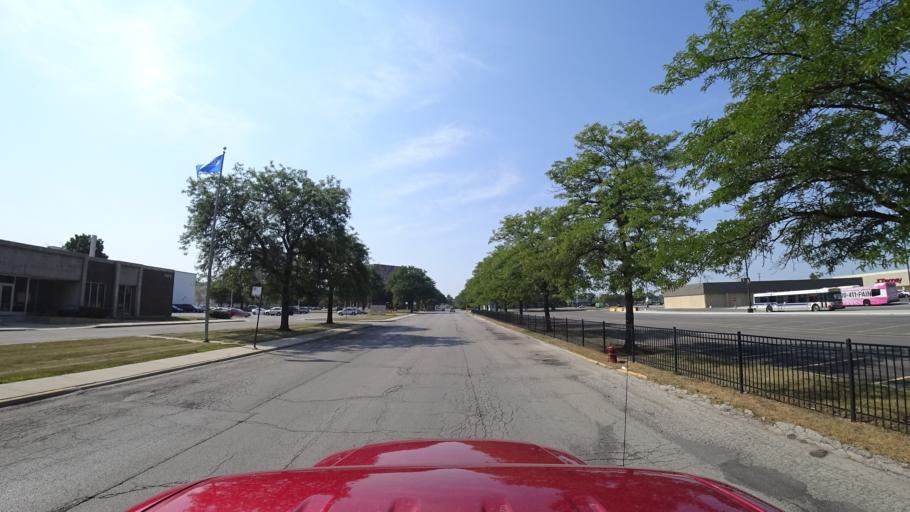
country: US
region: Illinois
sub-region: Cook County
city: Hometown
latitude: 41.7564
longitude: -87.7324
